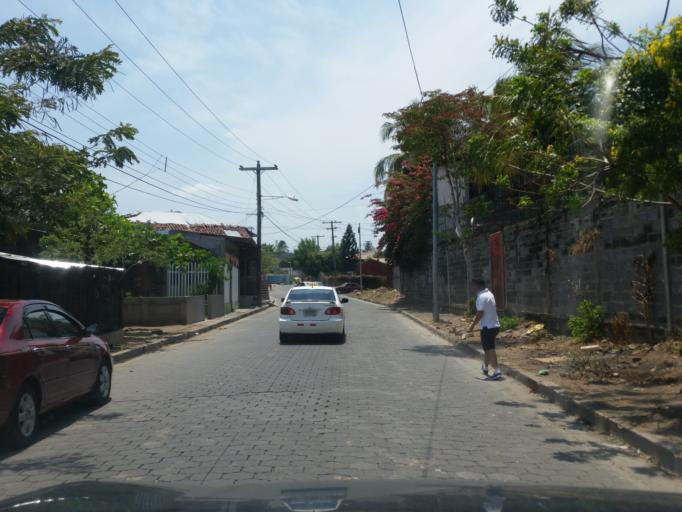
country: NI
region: Granada
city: Granada
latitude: 11.9291
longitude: -85.9469
